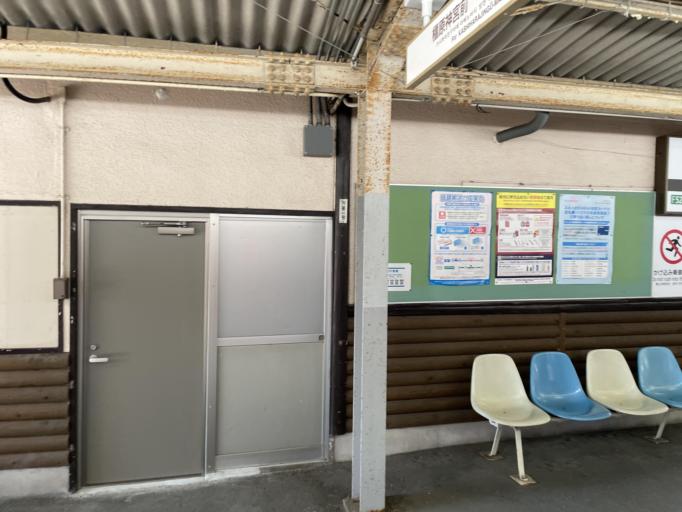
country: JP
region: Nara
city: Gose
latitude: 34.3882
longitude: 135.7664
